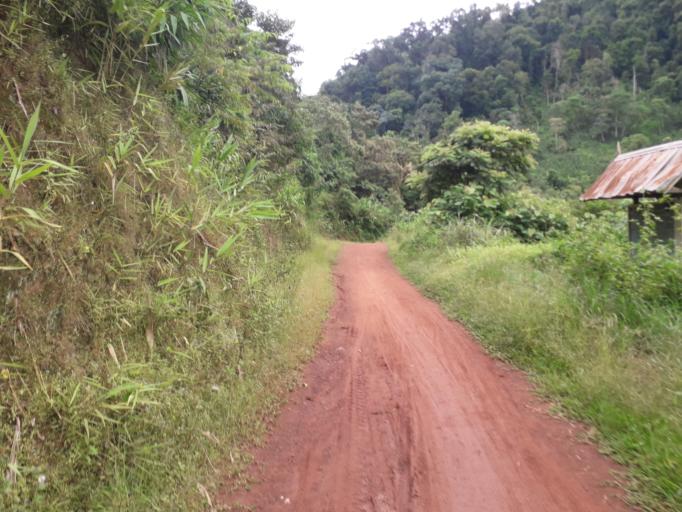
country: CN
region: Yunnan
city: Menglie
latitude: 22.2139
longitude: 101.6579
